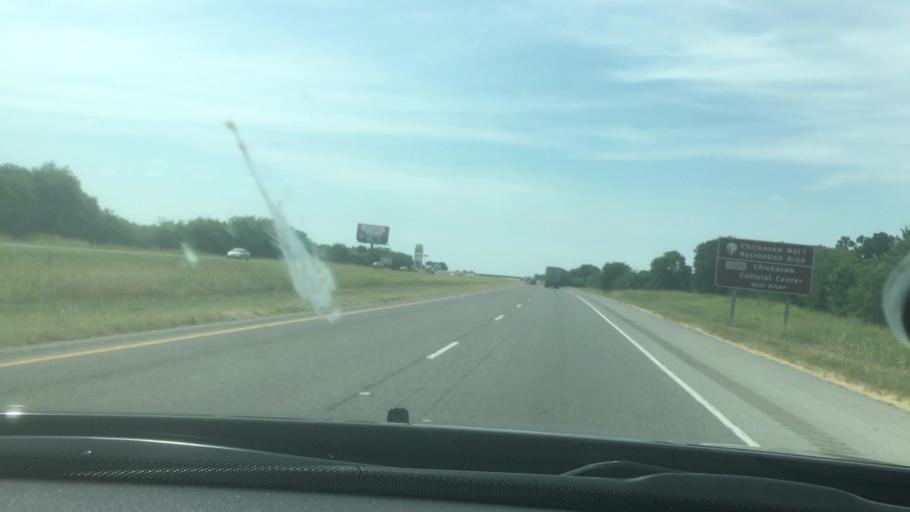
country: US
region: Oklahoma
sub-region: Murray County
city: Davis
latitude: 34.5170
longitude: -97.1816
